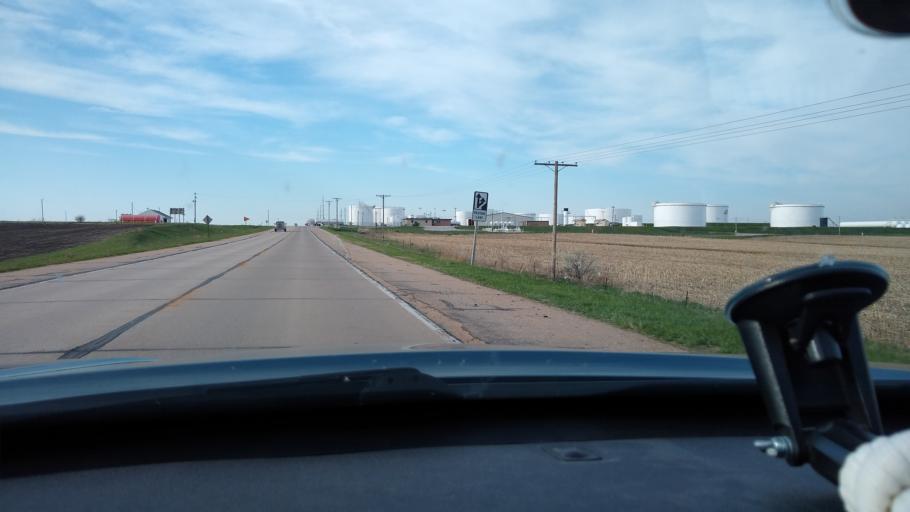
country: US
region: Nebraska
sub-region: Fillmore County
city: Geneva
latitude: 40.5475
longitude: -97.5958
